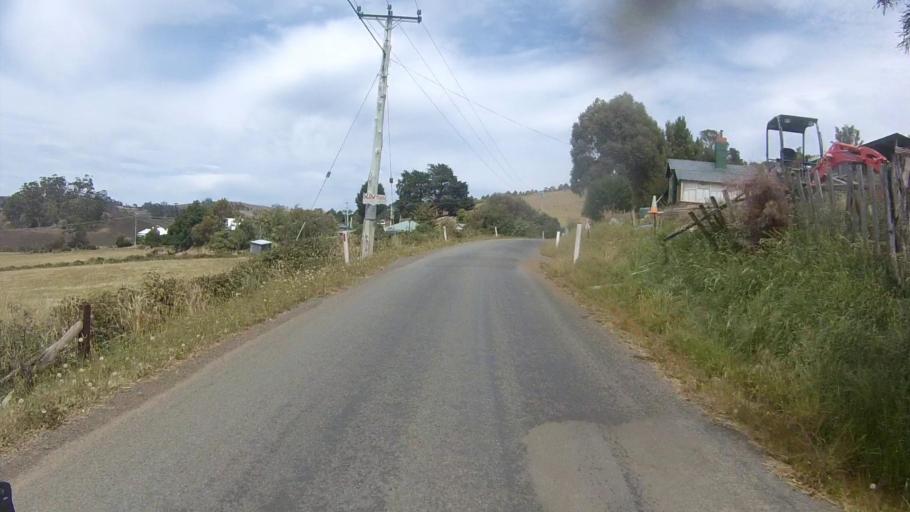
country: AU
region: Tasmania
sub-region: Sorell
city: Sorell
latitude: -42.8073
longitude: 147.8333
